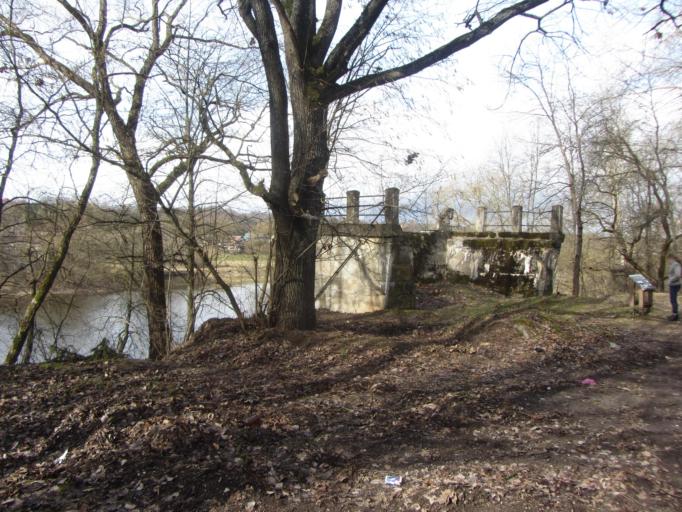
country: LT
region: Kauno apskritis
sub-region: Kauno rajonas
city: Akademija (Kaunas)
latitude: 54.9336
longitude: 23.7951
